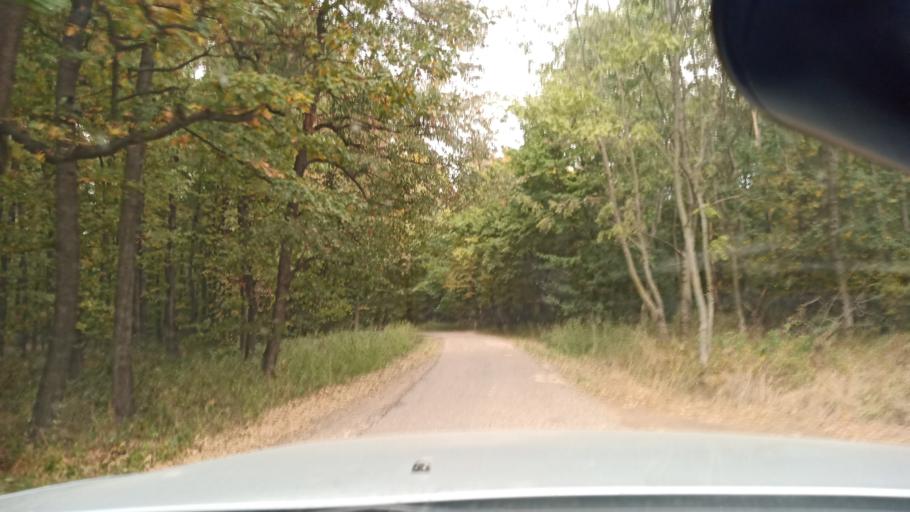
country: HU
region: Fejer
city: Pusztavam
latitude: 47.3799
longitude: 18.2756
